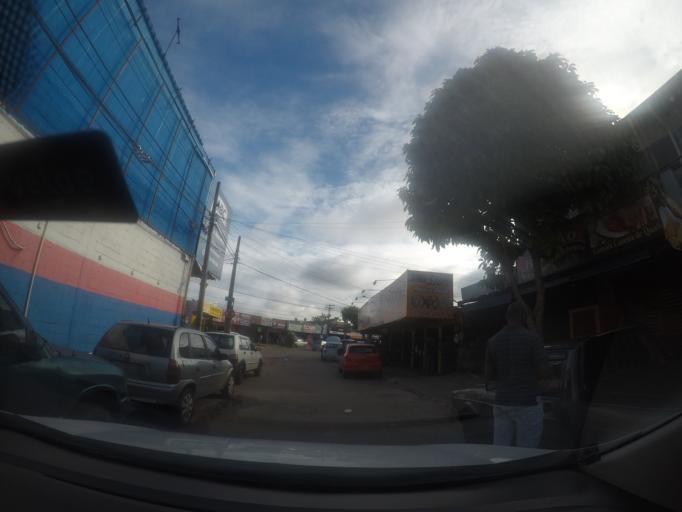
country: BR
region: Goias
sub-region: Goiania
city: Goiania
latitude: -16.6923
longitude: -49.3173
